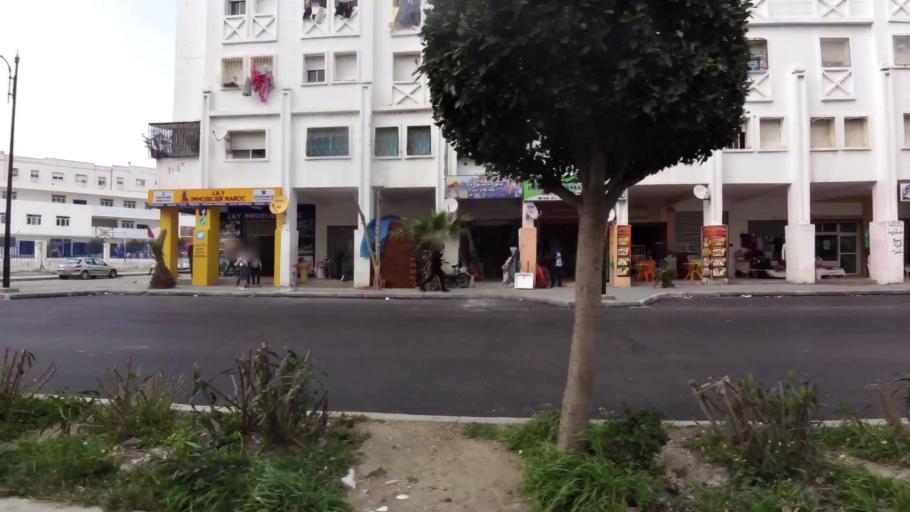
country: MA
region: Tanger-Tetouan
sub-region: Tanger-Assilah
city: Boukhalef
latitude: 35.7373
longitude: -5.8859
